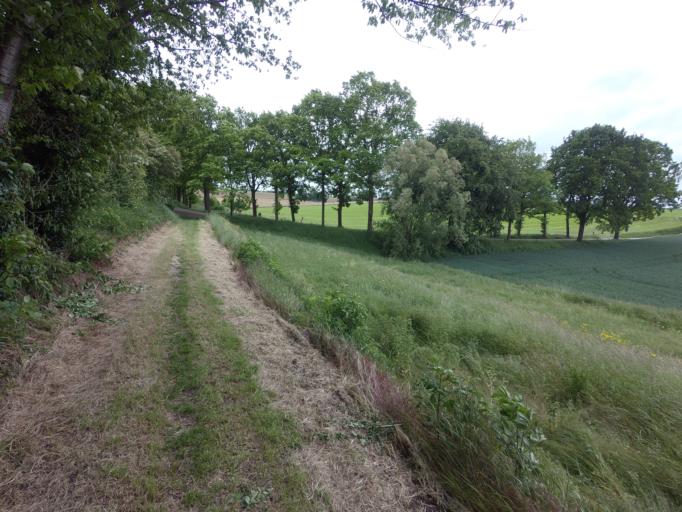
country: NL
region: Limburg
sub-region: Valkenburg aan de Geul
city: Schin op Geul
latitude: 50.8395
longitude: 5.9066
